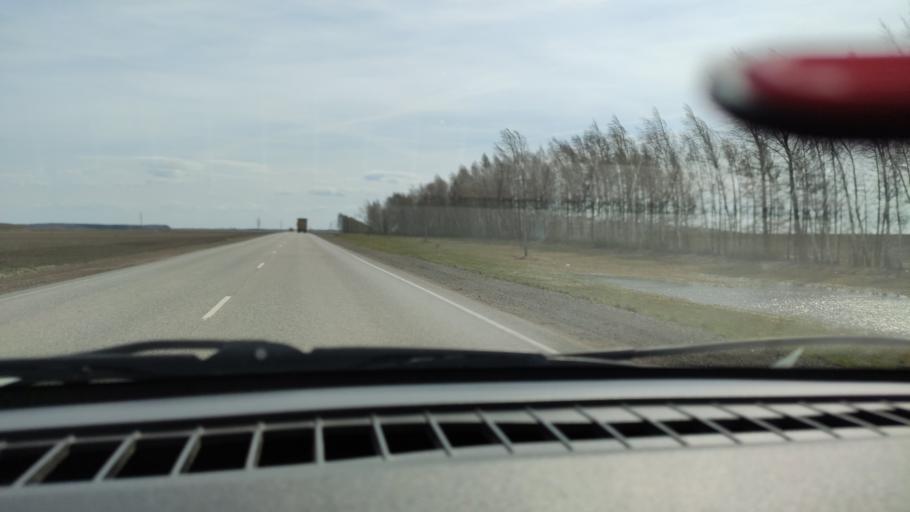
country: RU
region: Bashkortostan
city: Dyurtyuli
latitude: 55.3379
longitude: 54.9480
